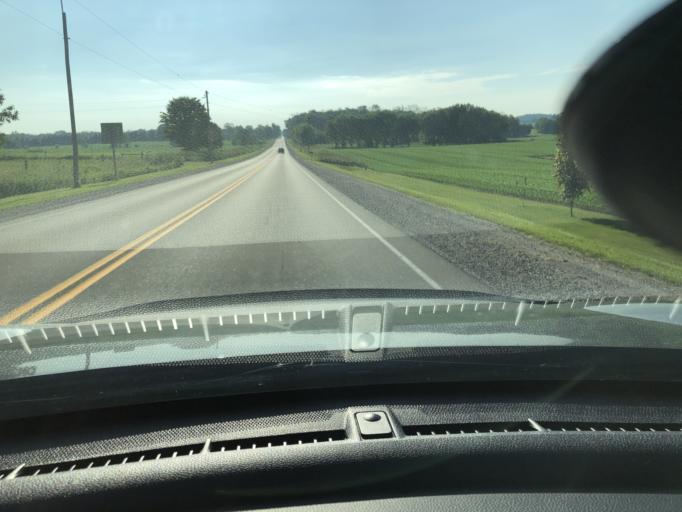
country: CA
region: Ontario
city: Stratford
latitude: 43.4250
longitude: -80.8368
